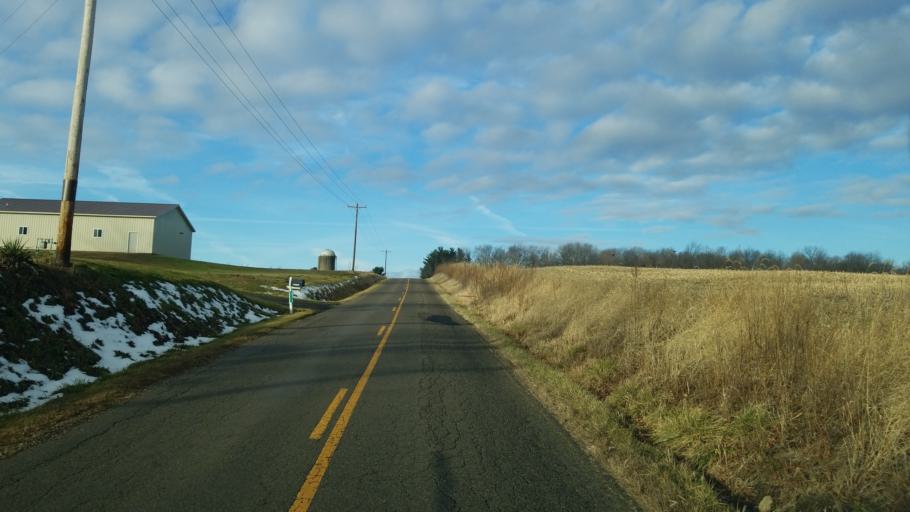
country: US
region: Ohio
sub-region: Knox County
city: Gambier
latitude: 40.3141
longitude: -82.3518
